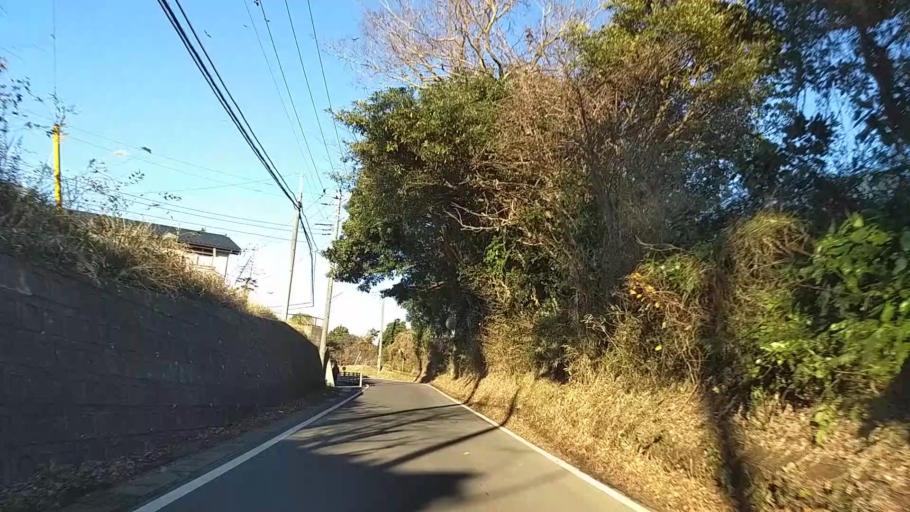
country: JP
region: Chiba
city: Hasaki
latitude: 35.7509
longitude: 140.7394
